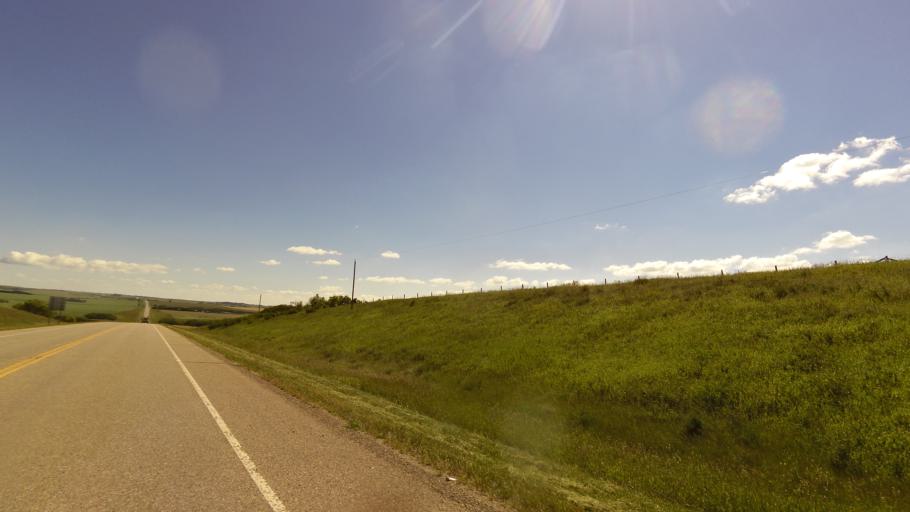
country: CA
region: Saskatchewan
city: Lloydminster
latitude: 52.8420
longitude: -110.0473
